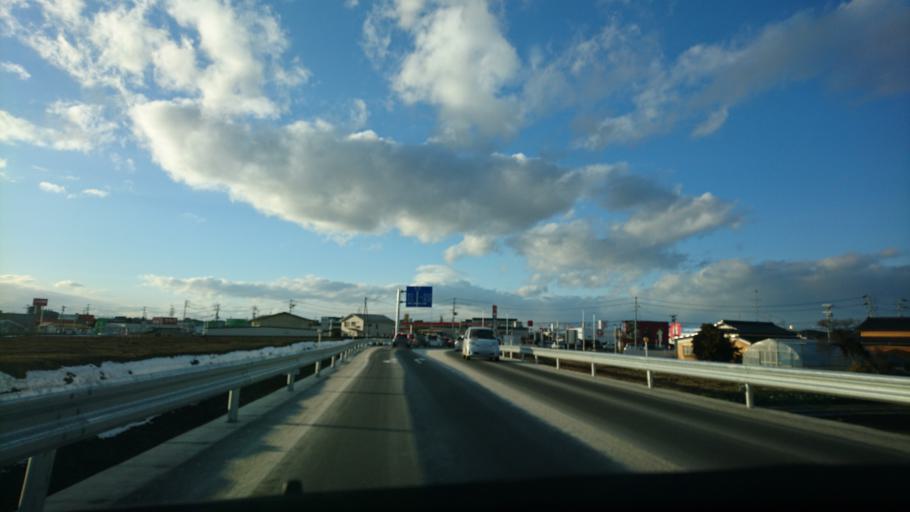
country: JP
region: Miyagi
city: Wakuya
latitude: 38.6959
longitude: 141.2140
